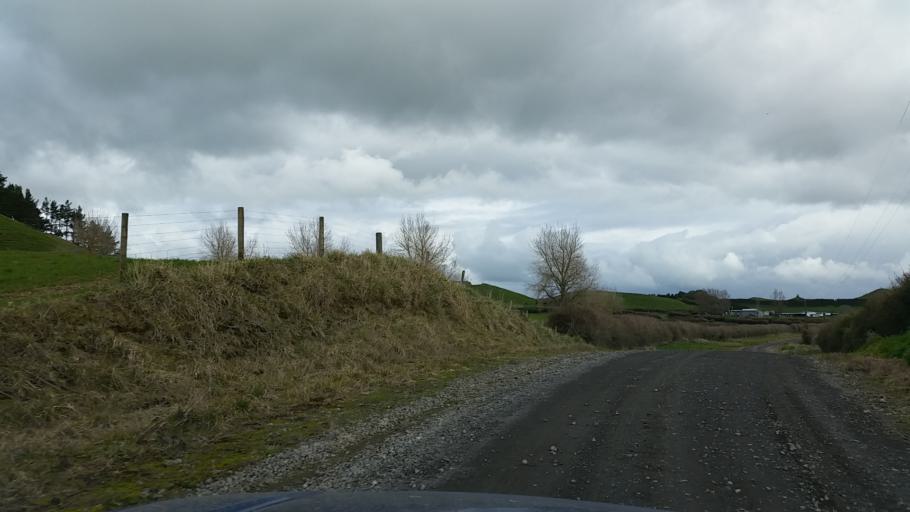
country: NZ
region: Taranaki
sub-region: South Taranaki District
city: Eltham
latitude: -39.3546
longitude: 174.3844
